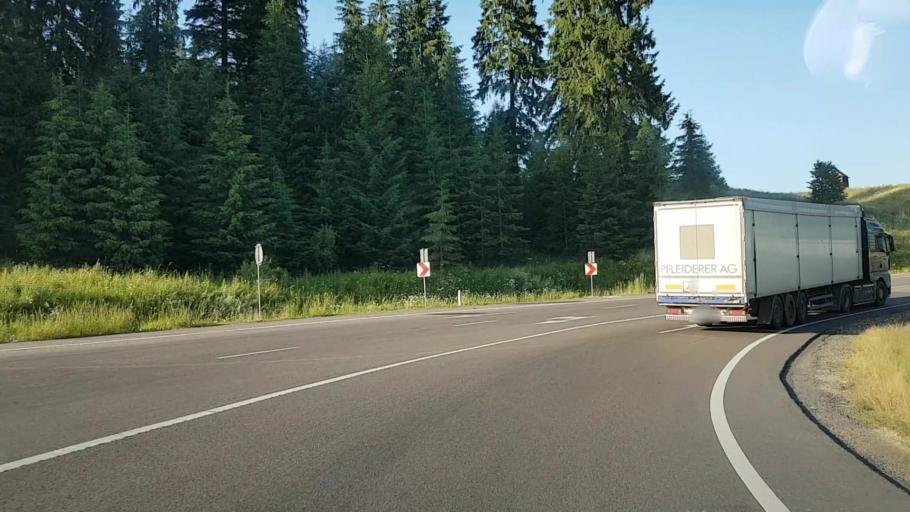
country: RO
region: Suceava
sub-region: Comuna Poiana Stampei
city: Poiana Stampei
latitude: 47.3003
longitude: 25.0957
